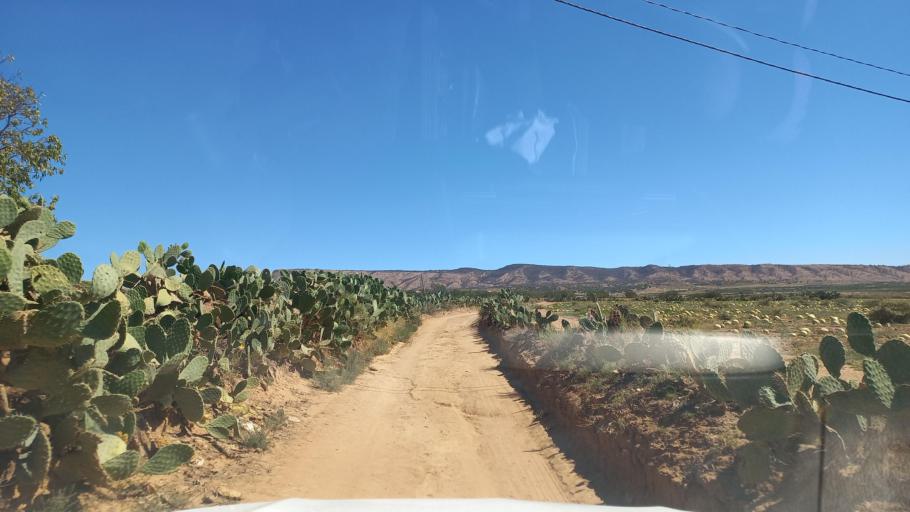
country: TN
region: Al Qasrayn
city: Sbiba
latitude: 35.3509
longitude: 9.1037
